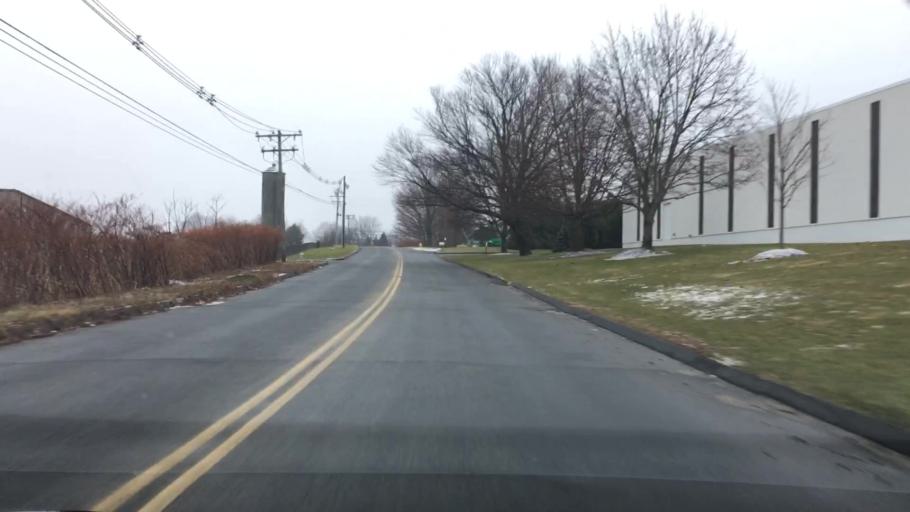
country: US
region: Connecticut
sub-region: Litchfield County
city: Oakville
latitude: 41.6124
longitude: -73.0904
